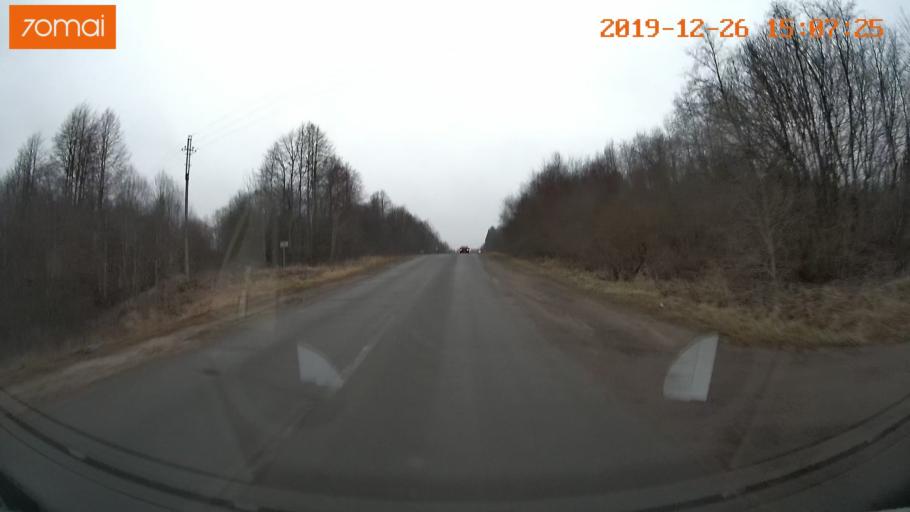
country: RU
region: Jaroslavl
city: Rybinsk
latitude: 58.1701
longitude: 38.8410
